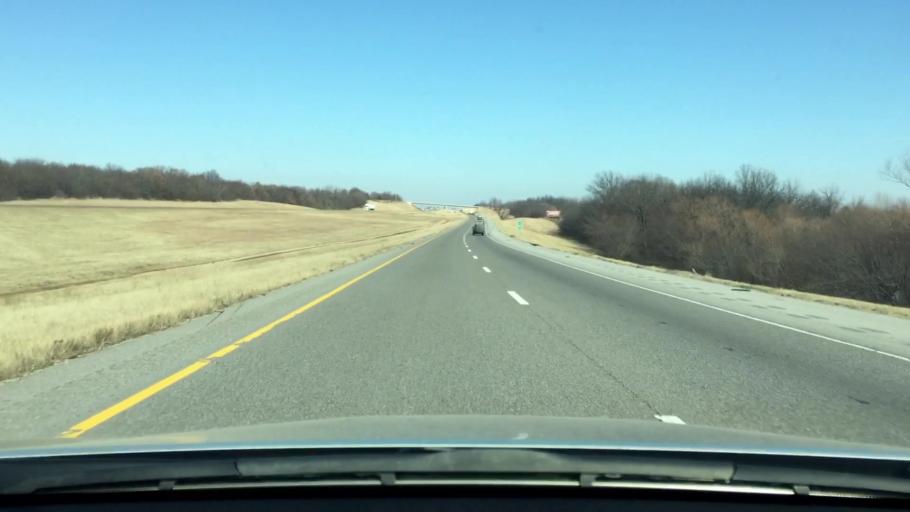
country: US
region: Oklahoma
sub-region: McClain County
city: Purcell
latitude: 34.9489
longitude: -97.3684
